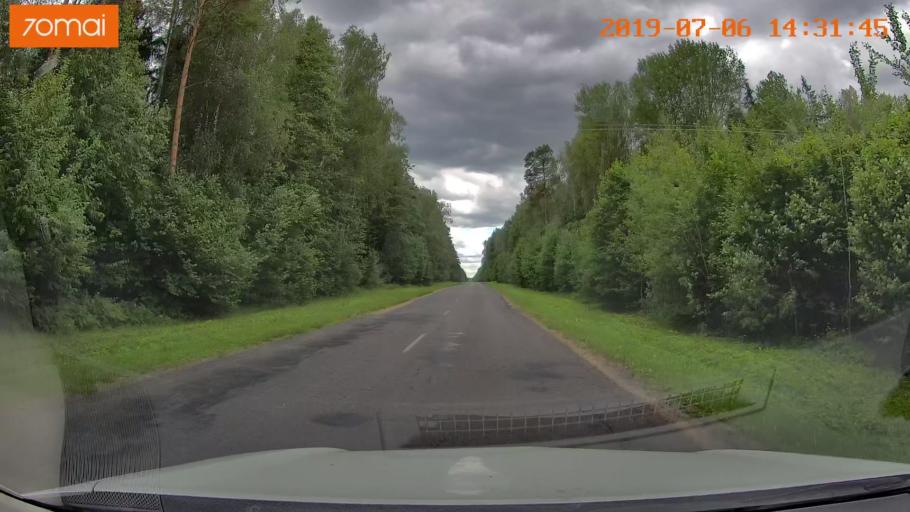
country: BY
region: Minsk
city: Ivyanyets
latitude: 53.9150
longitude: 26.7669
